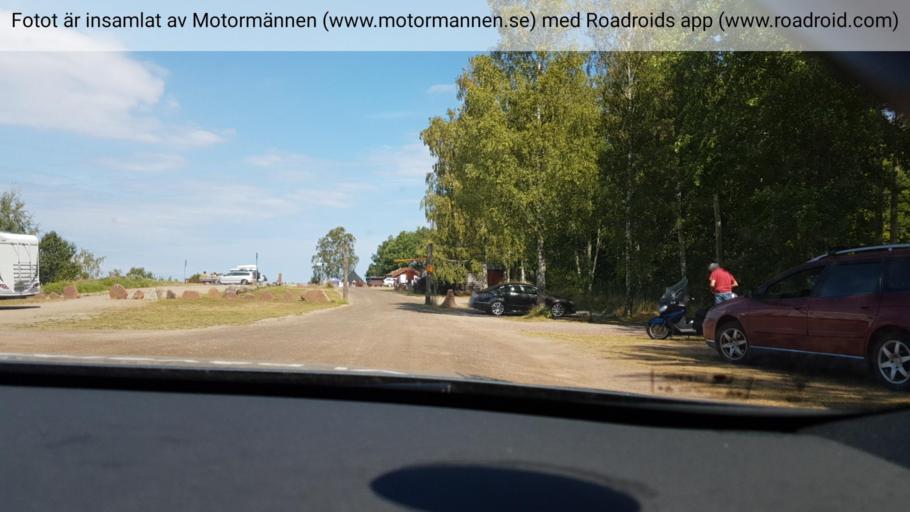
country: SE
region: Vaestra Goetaland
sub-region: Gotene Kommun
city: Goetene
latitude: 58.6184
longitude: 13.4021
